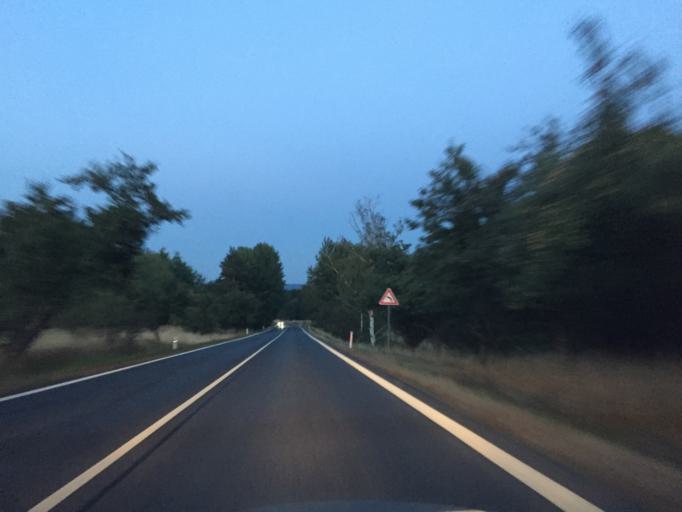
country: CZ
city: Brniste
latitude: 50.7726
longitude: 14.7026
